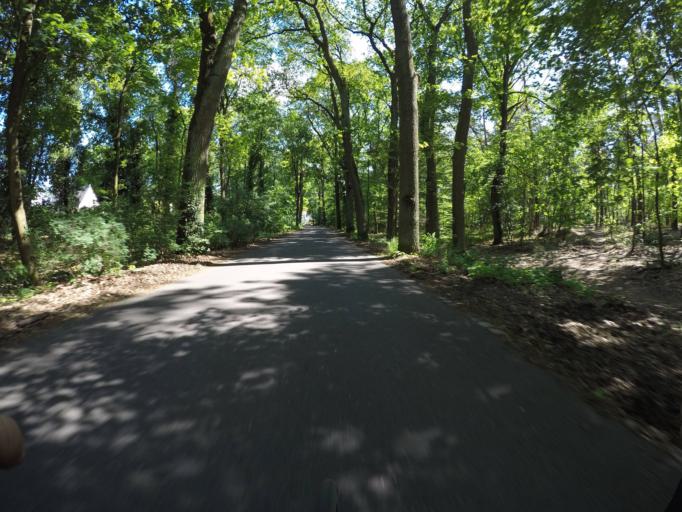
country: DE
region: Berlin
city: Wannsee
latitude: 52.4205
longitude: 13.1516
